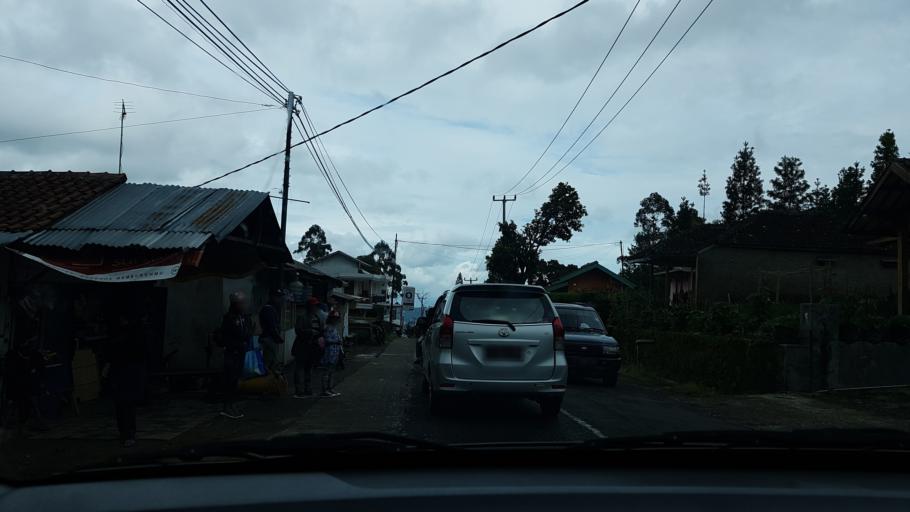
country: ID
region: West Java
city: Banjar
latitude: -7.1348
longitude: 107.4172
